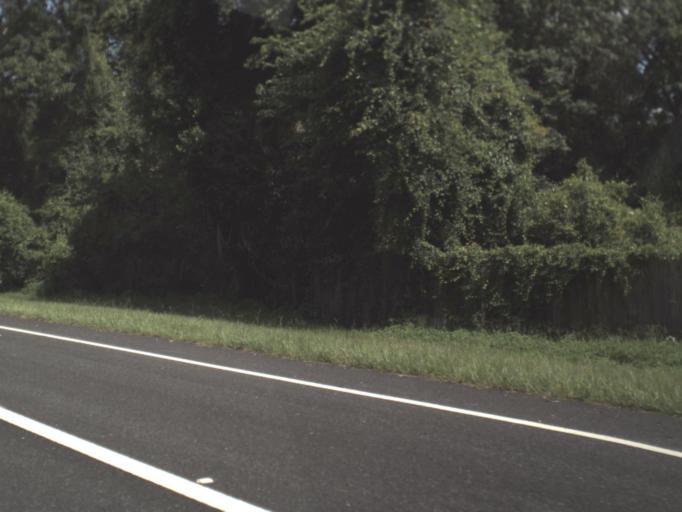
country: US
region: Florida
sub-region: Hernando County
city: Hill 'n Dale
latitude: 28.5344
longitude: -82.3344
